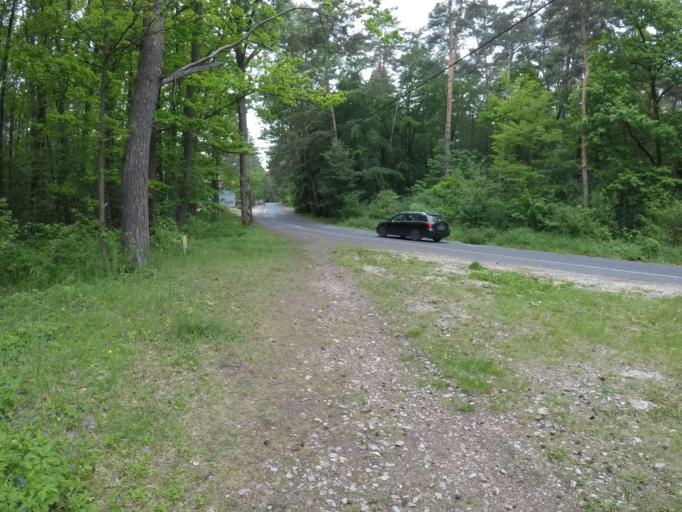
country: PL
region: Swietokrzyskie
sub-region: Powiat kielecki
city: Kielce
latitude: 50.8415
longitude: 20.6069
